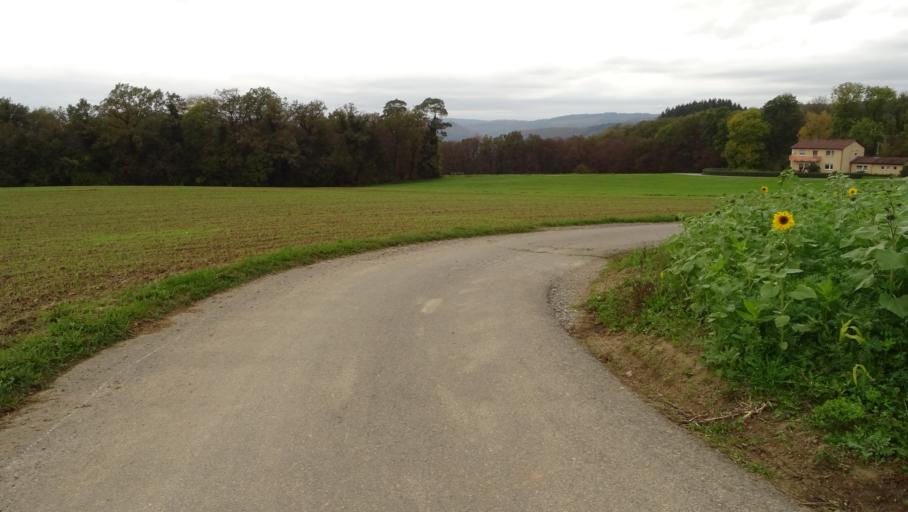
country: DE
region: Baden-Wuerttemberg
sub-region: Karlsruhe Region
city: Neckargerach
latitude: 49.3867
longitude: 9.0905
